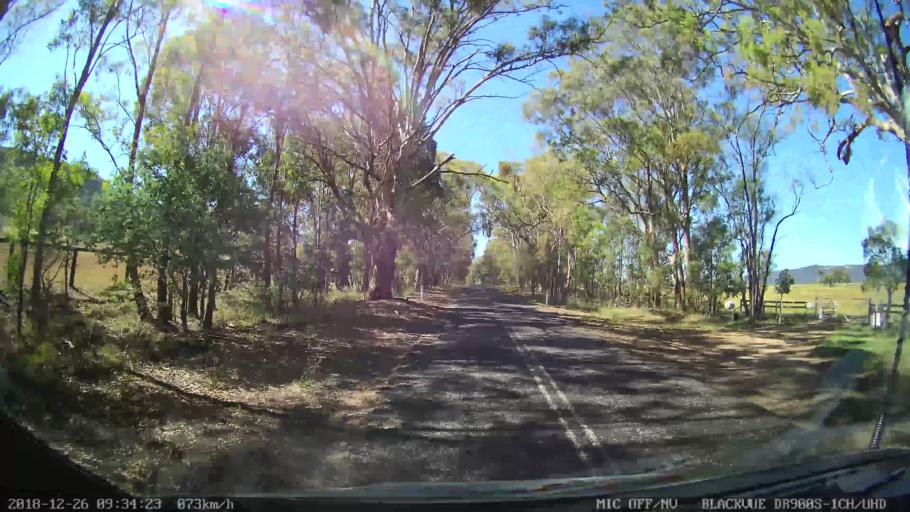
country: AU
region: New South Wales
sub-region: Mid-Western Regional
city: Kandos
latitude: -32.9047
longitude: 150.0379
